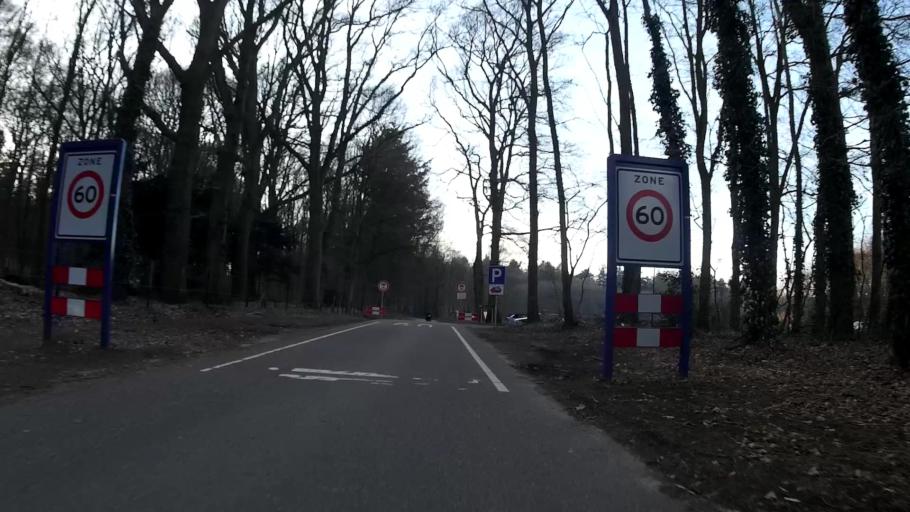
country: NL
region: Utrecht
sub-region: Gemeente Veenendaal
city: Veenendaal
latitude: 52.0064
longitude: 5.5381
